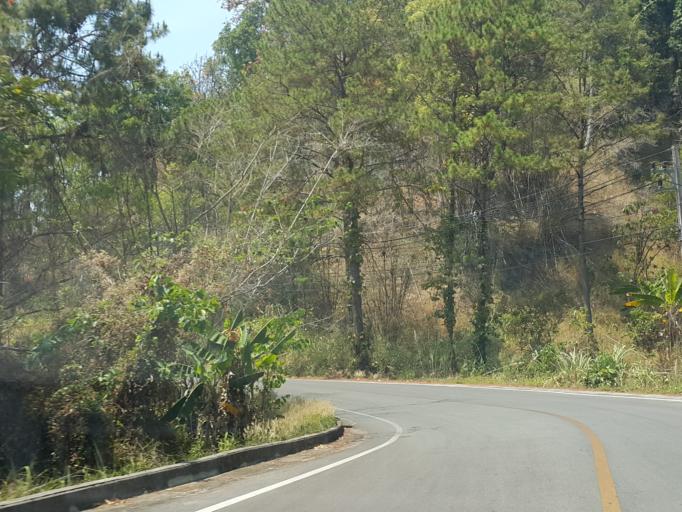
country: TH
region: Chiang Mai
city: Samoeng
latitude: 18.8718
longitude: 98.7834
